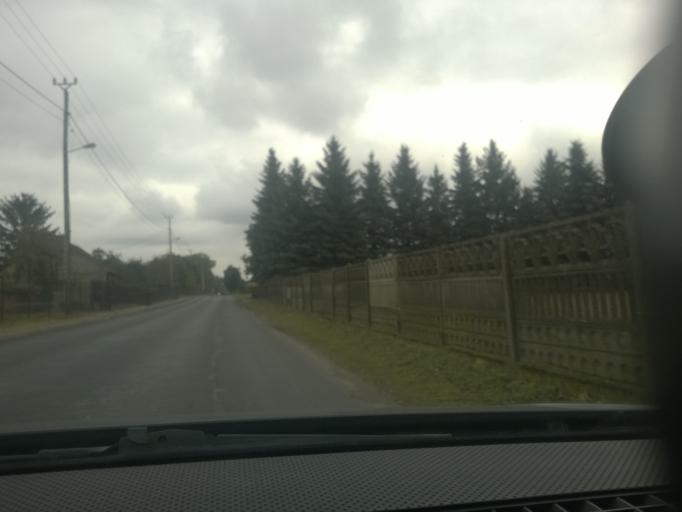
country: PL
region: Greater Poland Voivodeship
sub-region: Kalisz
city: Kalisz
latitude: 51.7263
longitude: 18.1388
